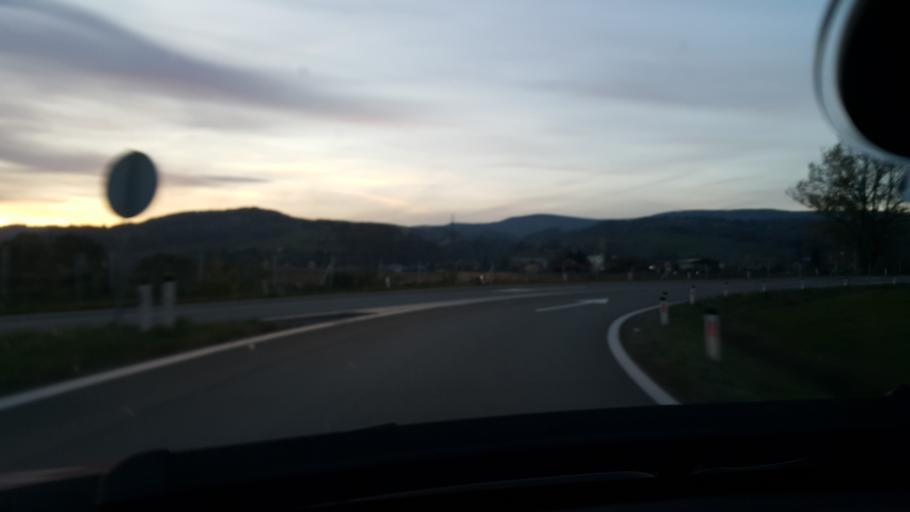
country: SI
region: Race-Fram
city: Fram
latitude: 46.4498
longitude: 15.6489
